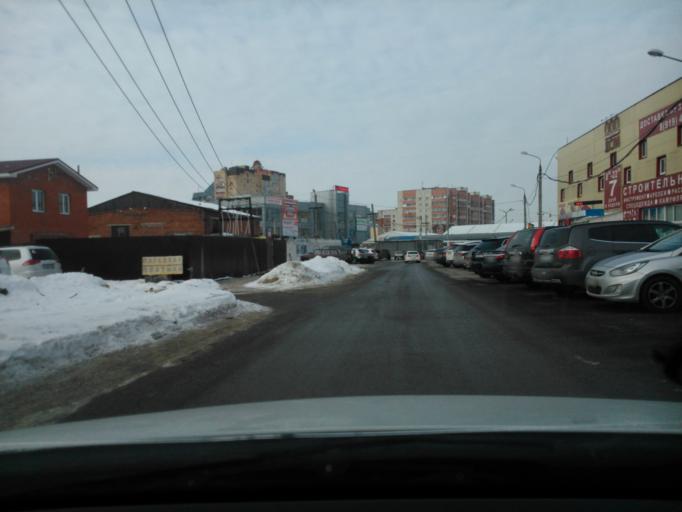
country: RU
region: Perm
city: Perm
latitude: 58.0012
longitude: 56.2248
